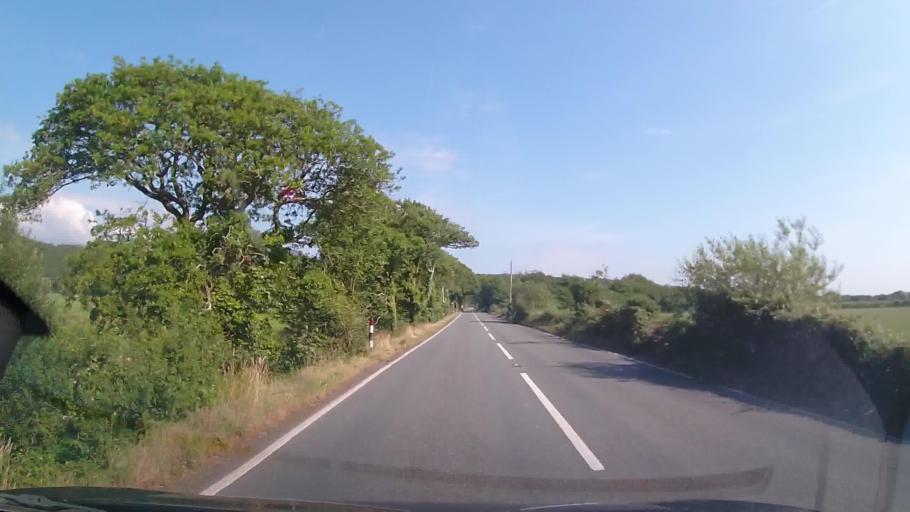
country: GB
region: Wales
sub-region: Gwynedd
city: Llanbedr
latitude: 52.8283
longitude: -4.1079
